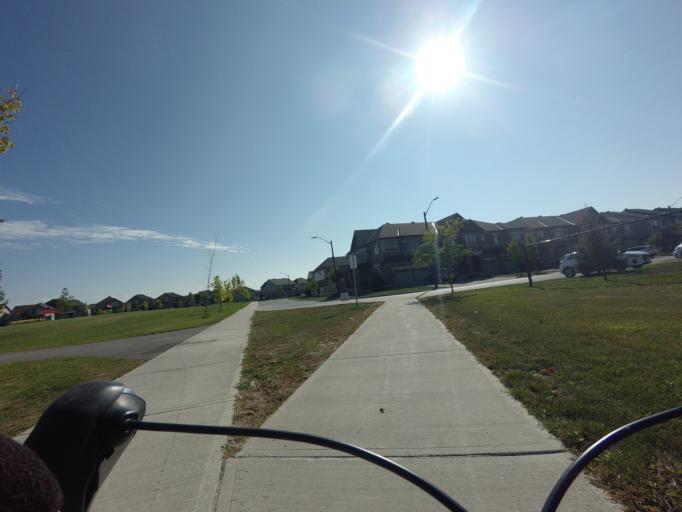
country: CA
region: Ontario
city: Bells Corners
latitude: 45.2679
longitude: -75.6963
